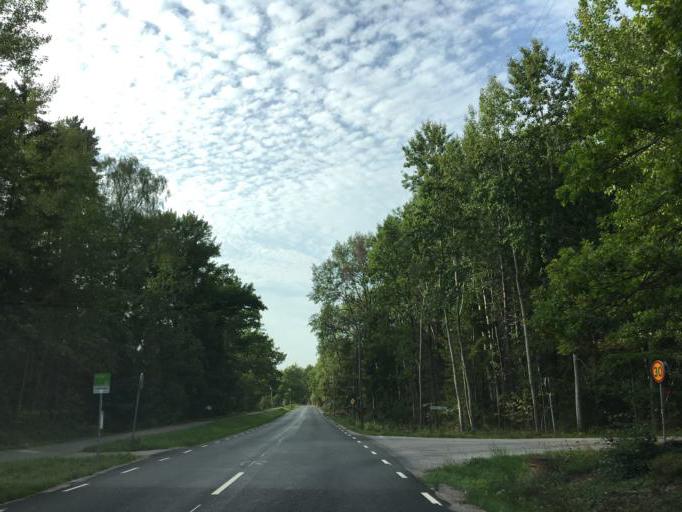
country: SE
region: Soedermanland
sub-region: Eskilstuna Kommun
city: Torshalla
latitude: 59.4482
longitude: 16.4465
